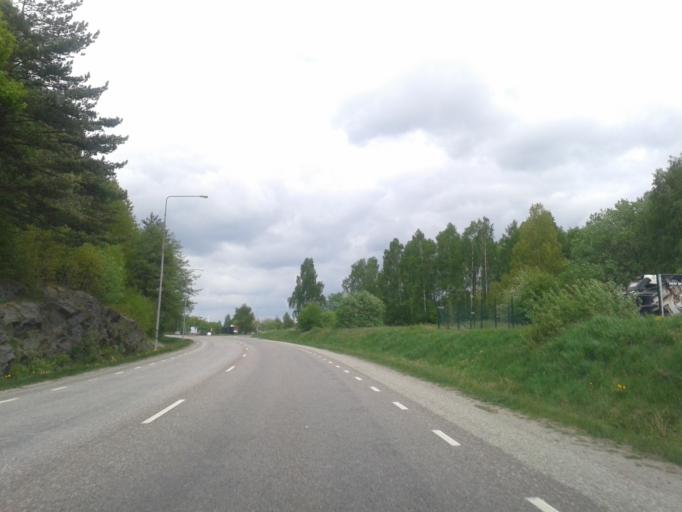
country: SE
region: Vaestra Goetaland
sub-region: Goteborg
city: Eriksbo
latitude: 57.7804
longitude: 12.0486
